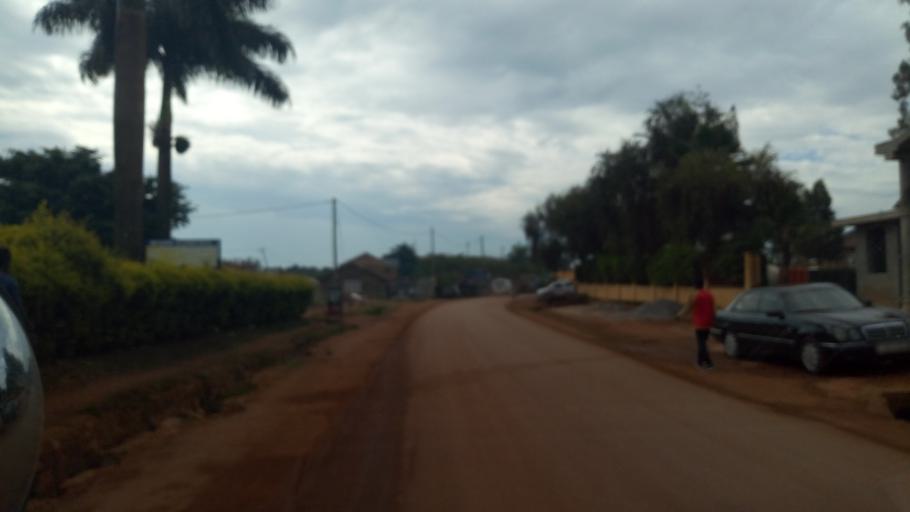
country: UG
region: Central Region
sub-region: Mukono District
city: Mukono
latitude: 0.3663
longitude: 32.7141
